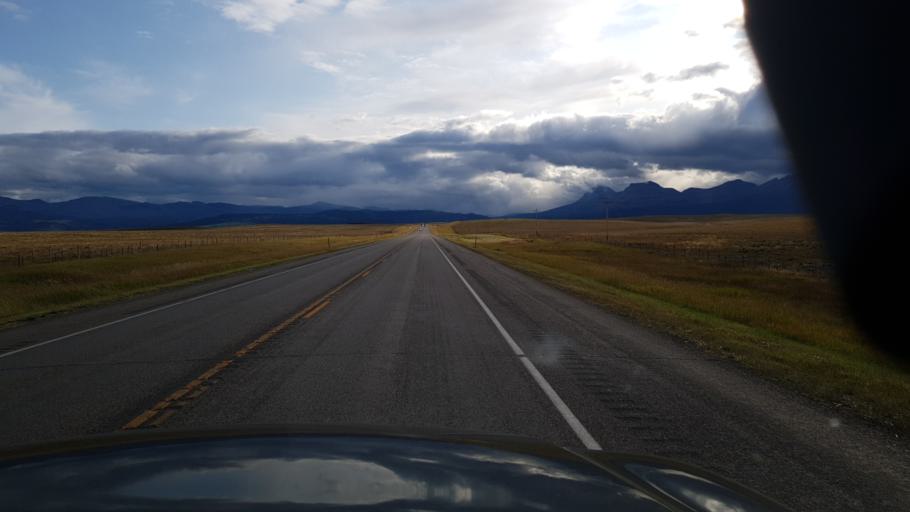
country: US
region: Montana
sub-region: Glacier County
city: South Browning
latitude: 48.4799
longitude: -113.1397
